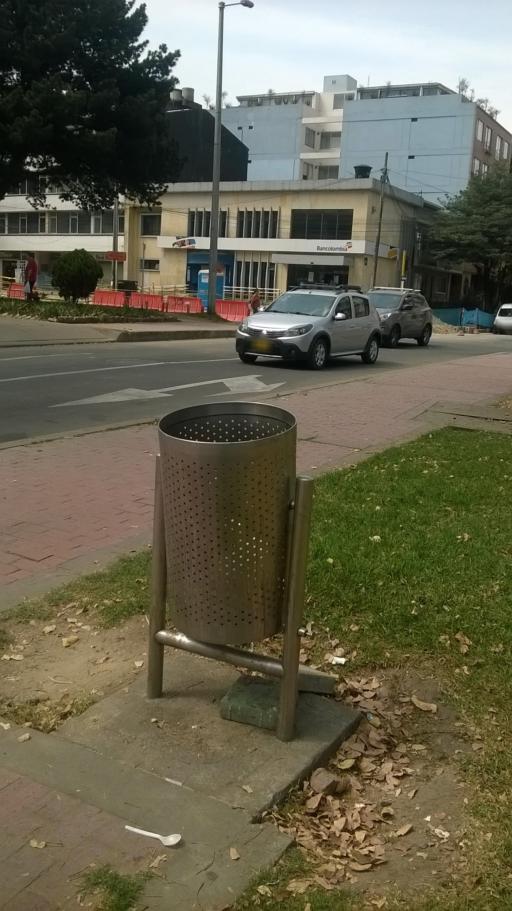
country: CO
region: Bogota D.C.
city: Bogota
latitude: 4.6317
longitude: -74.0750
